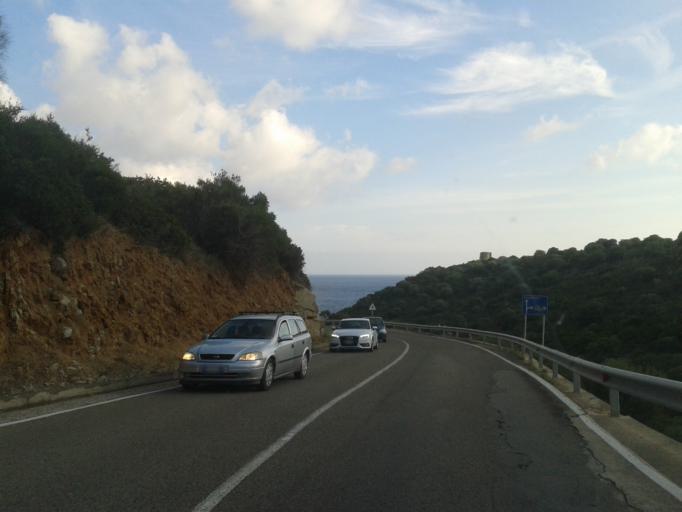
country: IT
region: Sardinia
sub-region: Provincia di Cagliari
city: Quartu Sant'Elena
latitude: 39.1815
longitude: 9.3532
